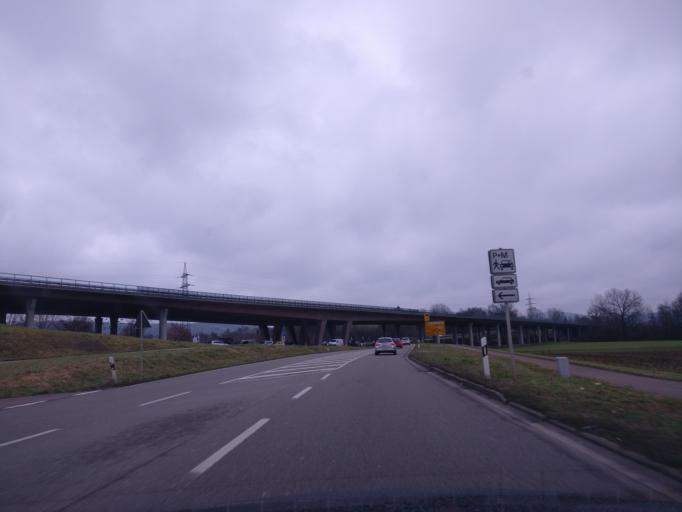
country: DE
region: Baden-Wuerttemberg
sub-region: Regierungsbezirk Stuttgart
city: Schorndorf
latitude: 48.8186
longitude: 9.5438
